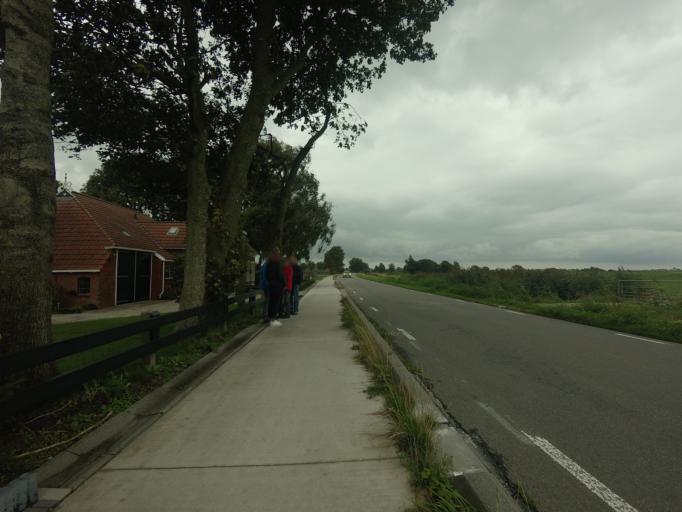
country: NL
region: Friesland
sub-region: Sudwest Fryslan
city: Heeg
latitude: 52.9907
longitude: 5.5691
